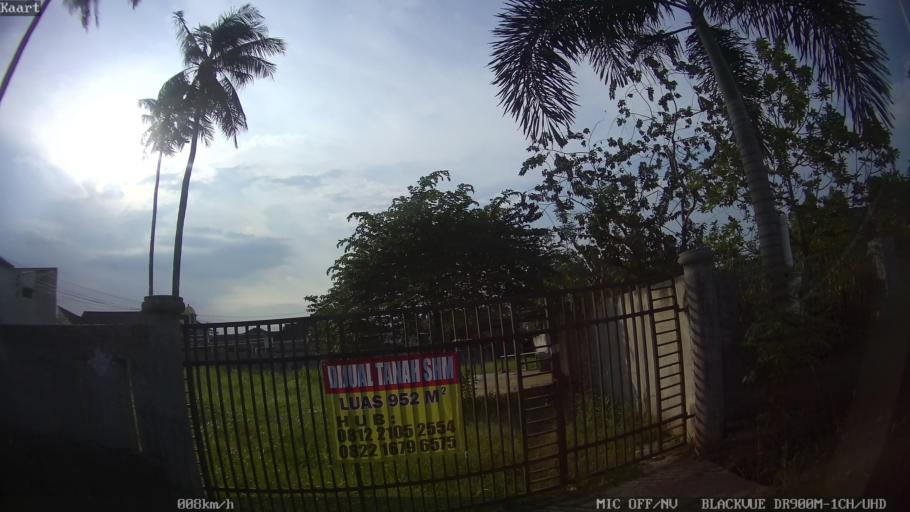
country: ID
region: Lampung
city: Kedaton
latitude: -5.3772
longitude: 105.2406
